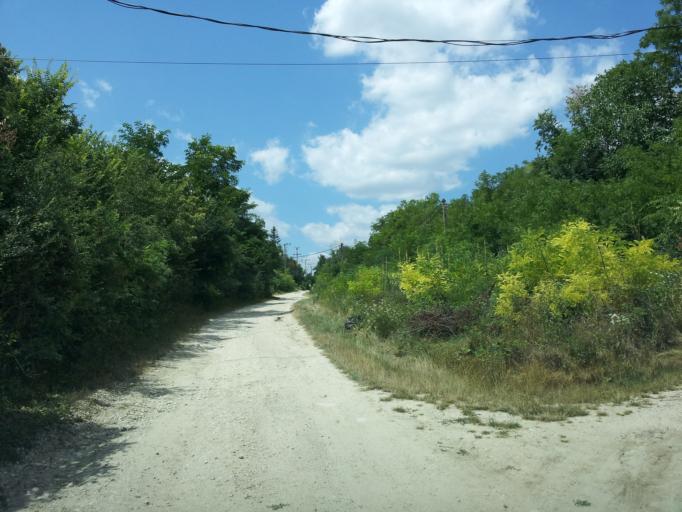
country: HU
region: Veszprem
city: Balatonkenese
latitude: 47.0405
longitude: 18.0936
